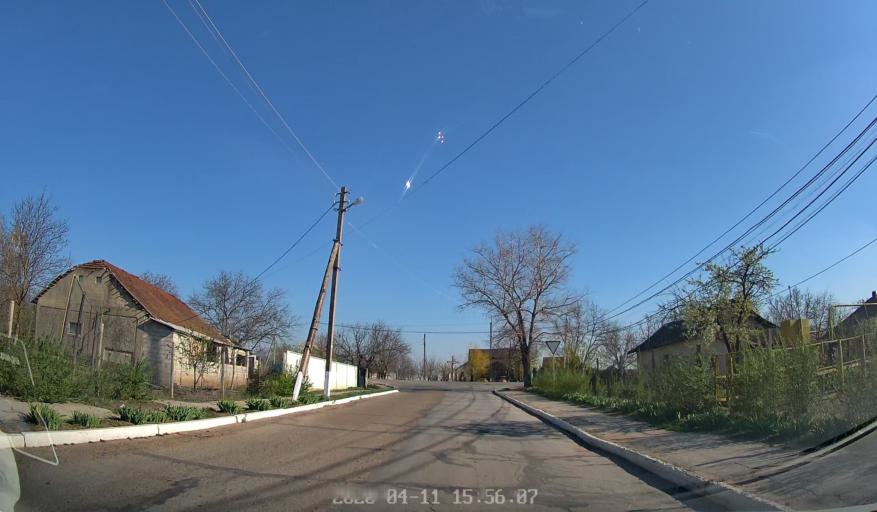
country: MD
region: Chisinau
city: Vadul lui Voda
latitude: 47.0937
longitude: 29.1785
